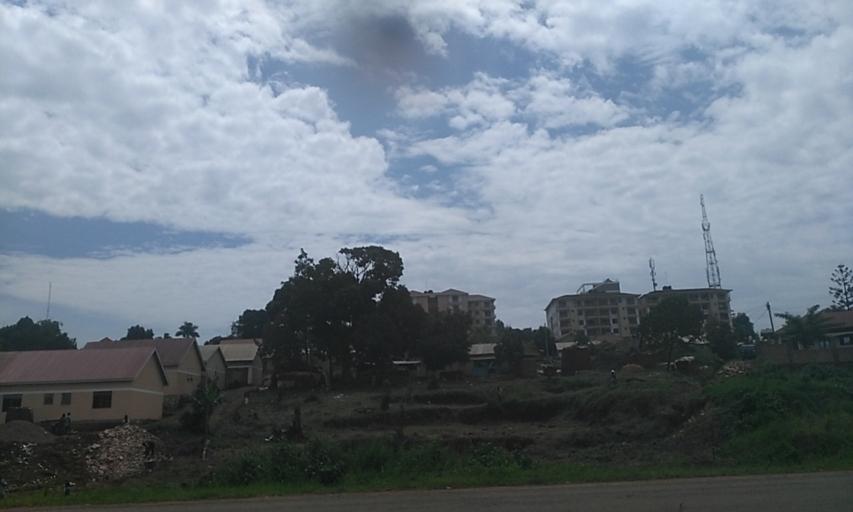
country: UG
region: Central Region
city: Kampala Central Division
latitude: 0.3587
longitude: 32.5971
